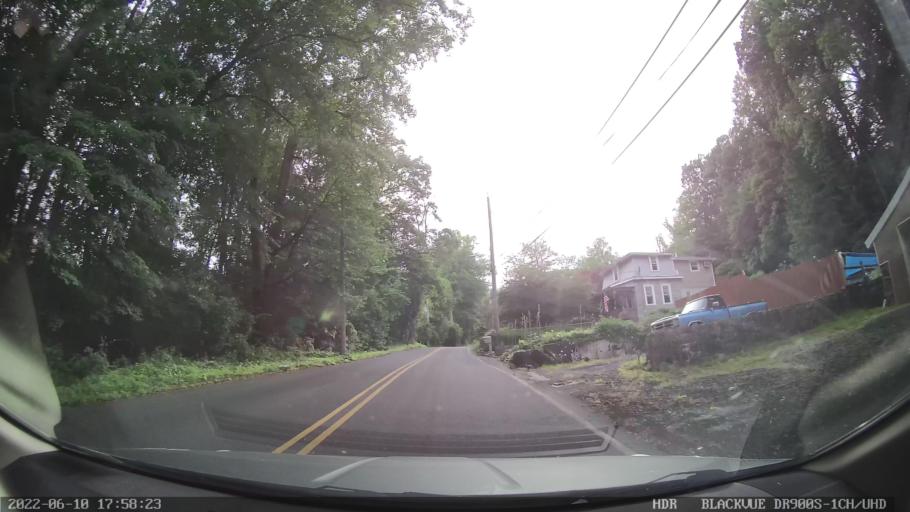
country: US
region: Pennsylvania
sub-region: Berks County
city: Pennside
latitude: 40.3397
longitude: -75.8865
